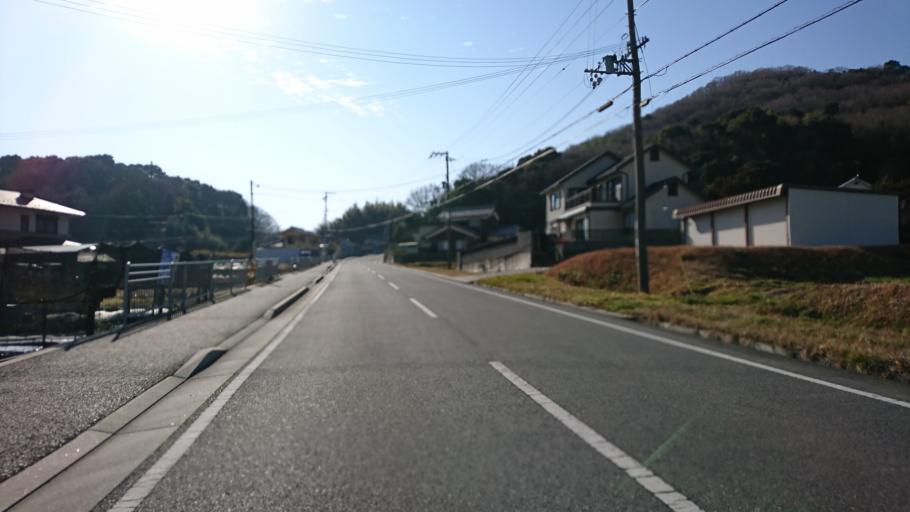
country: JP
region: Hyogo
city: Kakogawacho-honmachi
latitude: 34.8276
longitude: 134.8301
